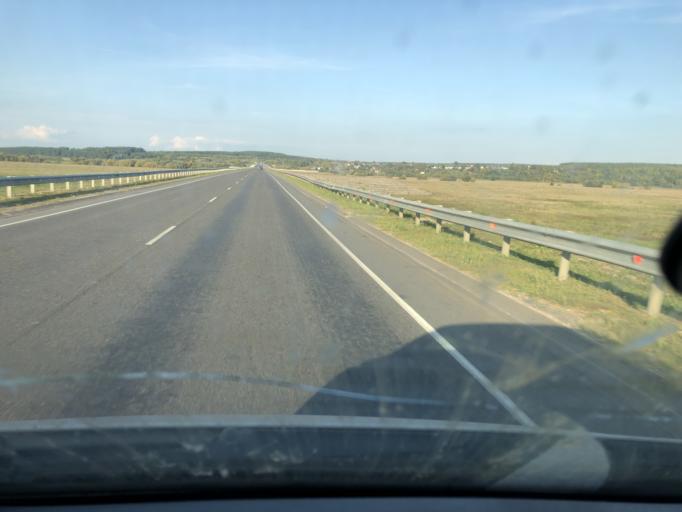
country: RU
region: Kaluga
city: Peremyshl'
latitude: 54.2850
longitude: 36.1586
